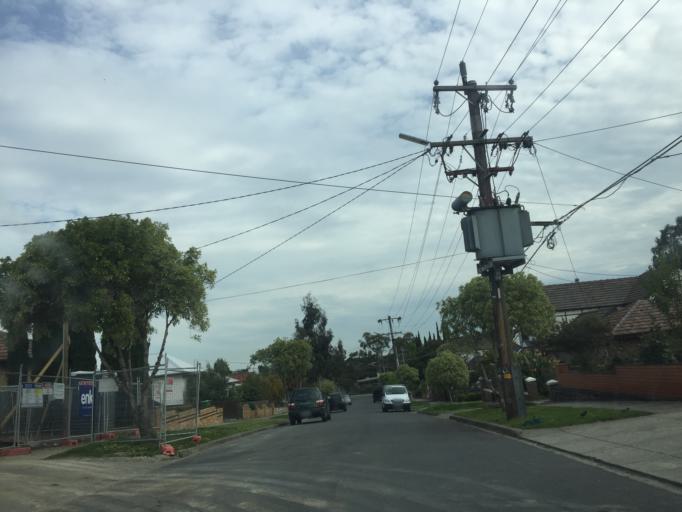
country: AU
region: Victoria
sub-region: Darebin
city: Preston
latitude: -37.7566
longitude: 145.0201
